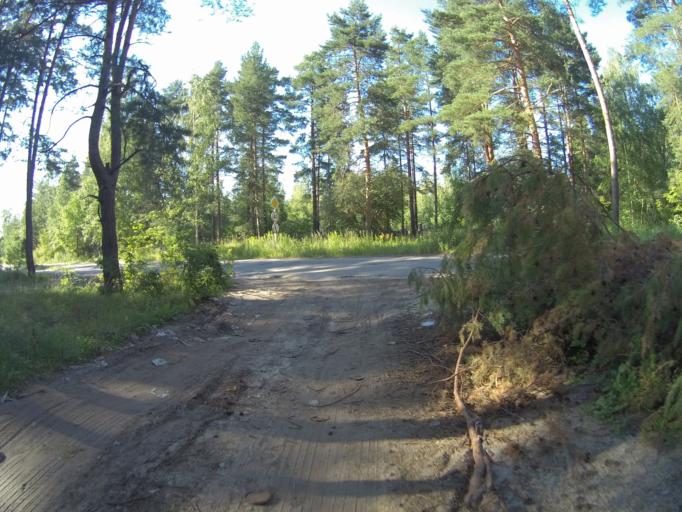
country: RU
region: Vladimir
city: Golovino
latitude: 56.0350
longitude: 40.4326
